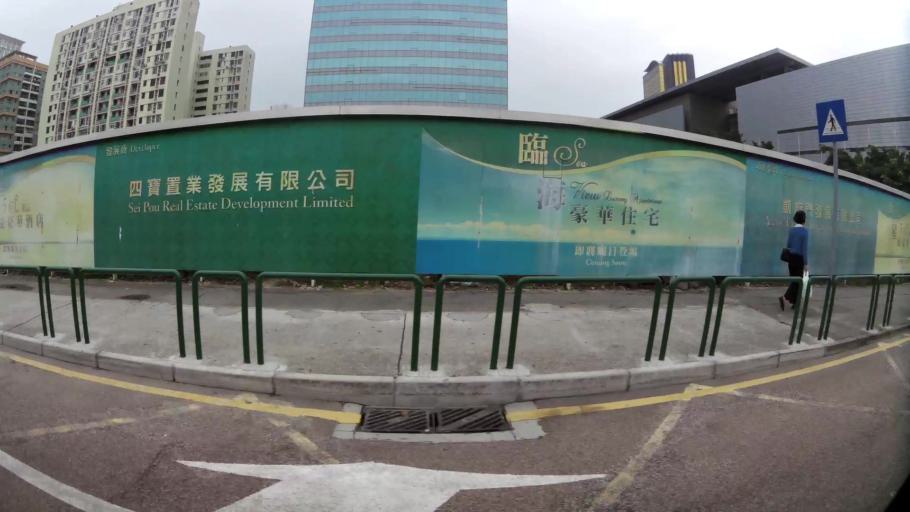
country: MO
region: Macau
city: Macau
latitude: 22.1877
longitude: 113.5543
